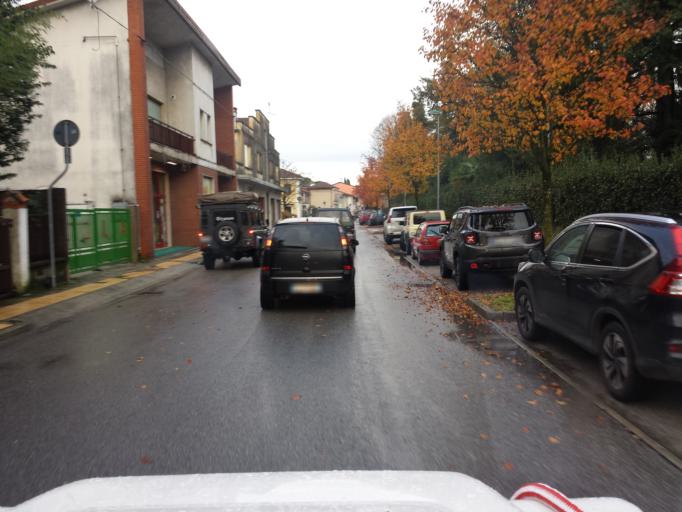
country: IT
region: Friuli Venezia Giulia
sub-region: Provincia di Gorizia
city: Gradisca d'Isonzo
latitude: 45.8891
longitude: 13.4989
